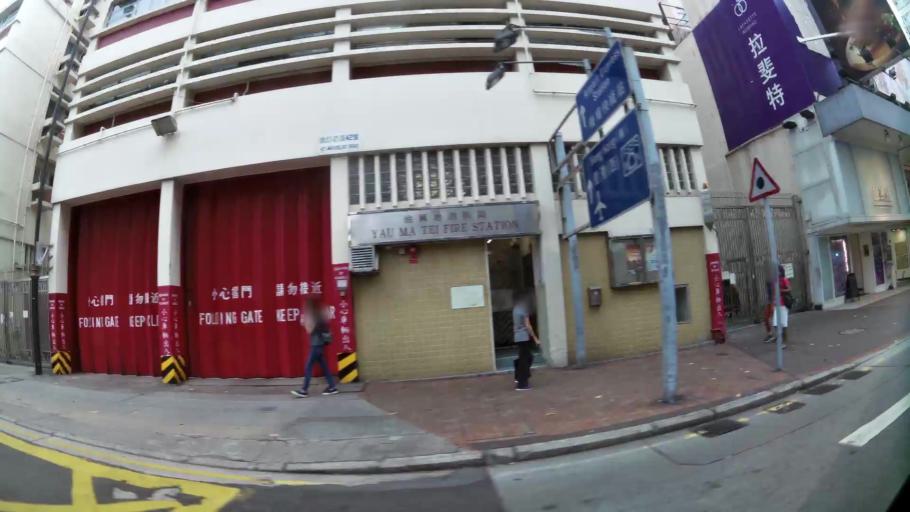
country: HK
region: Kowloon City
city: Kowloon
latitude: 22.3130
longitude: 114.1713
